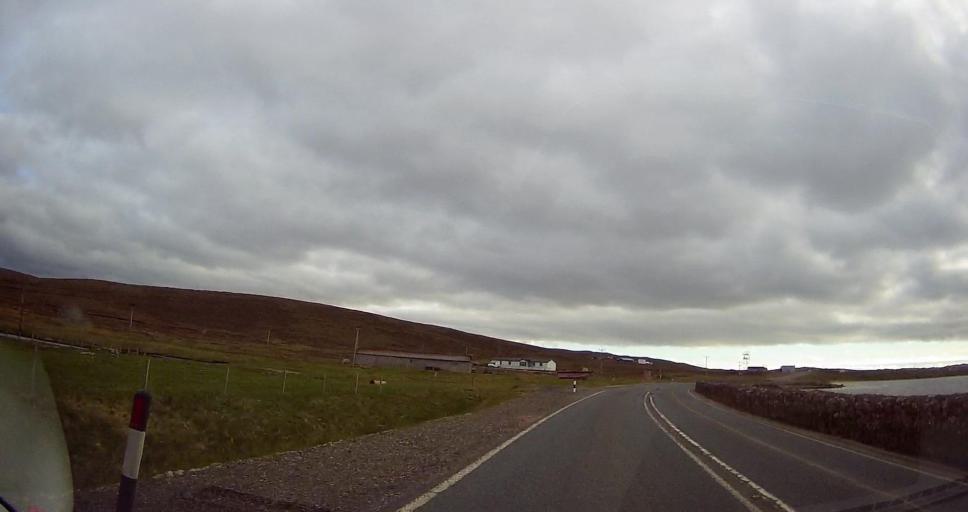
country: GB
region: Scotland
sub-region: Shetland Islands
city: Lerwick
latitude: 60.4435
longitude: -1.2594
